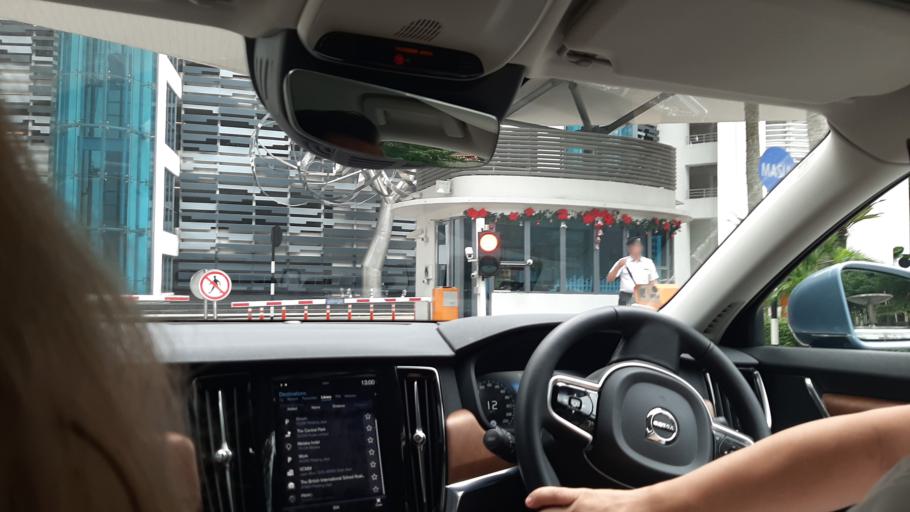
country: MY
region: Kuala Lumpur
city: Kuala Lumpur
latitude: 3.1696
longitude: 101.6553
